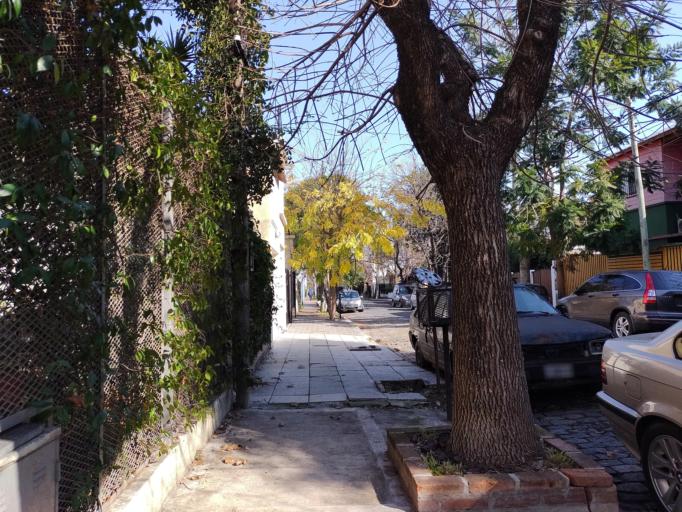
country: AR
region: Buenos Aires
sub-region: Partido de San Isidro
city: San Isidro
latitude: -34.4501
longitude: -58.5369
